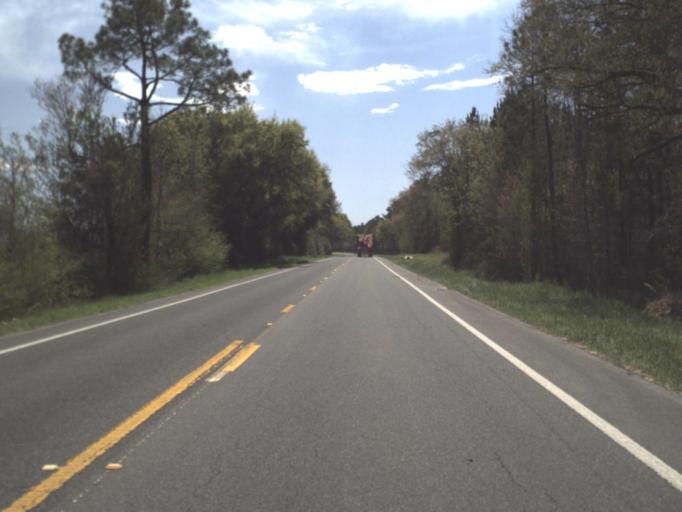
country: US
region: Florida
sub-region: Walton County
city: DeFuniak Springs
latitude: 30.8261
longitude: -85.9562
